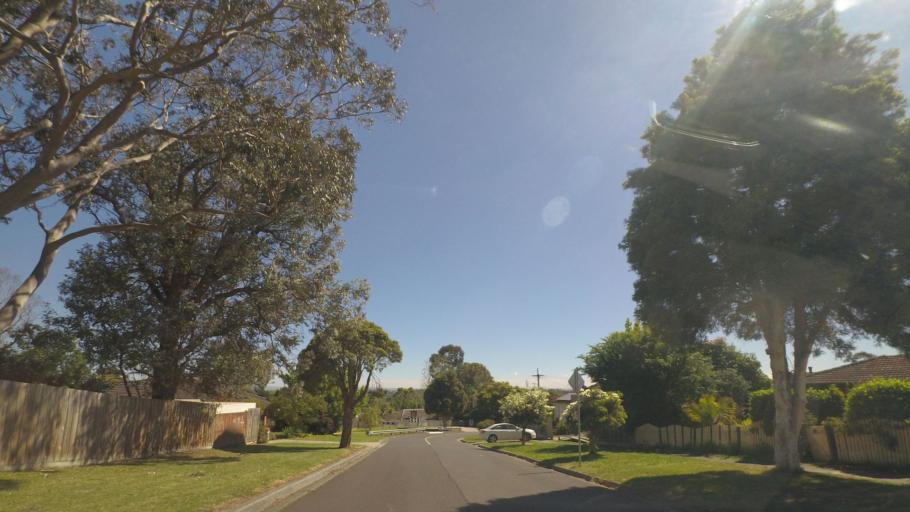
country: AU
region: Victoria
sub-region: Yarra Ranges
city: Kilsyth
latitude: -37.7986
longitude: 145.3087
